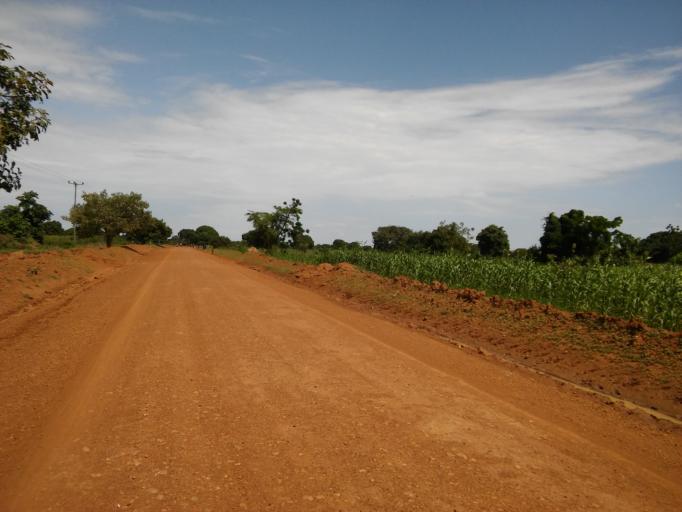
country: UG
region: Eastern Region
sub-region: Kumi District
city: Kumi
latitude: 1.4771
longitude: 33.8841
